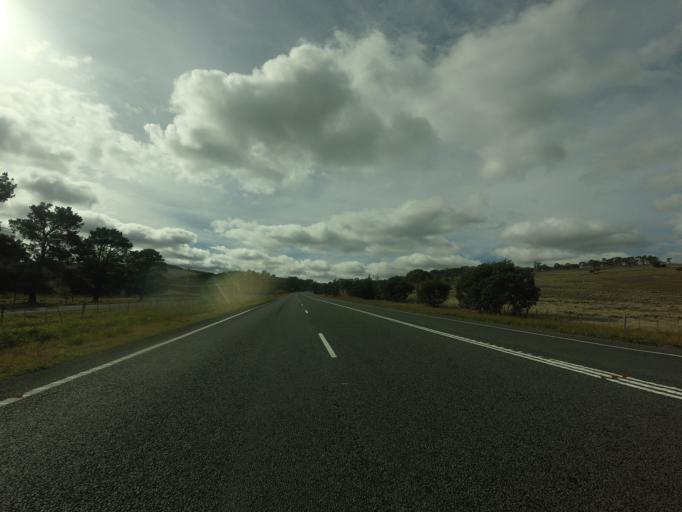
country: AU
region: Tasmania
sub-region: Brighton
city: Bridgewater
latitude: -42.4578
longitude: 147.1949
